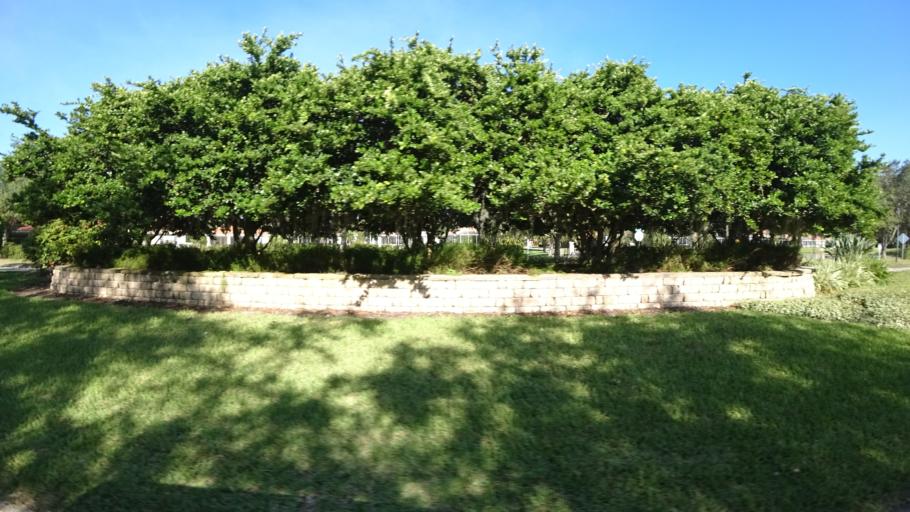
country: US
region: Florida
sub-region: Sarasota County
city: Desoto Lakes
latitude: 27.4185
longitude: -82.4655
